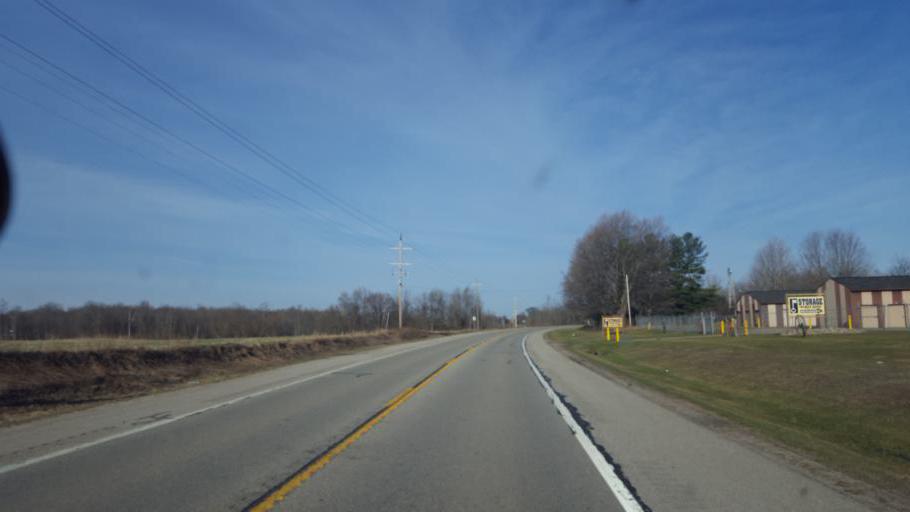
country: US
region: Michigan
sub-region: Montcalm County
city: Edmore
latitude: 43.4080
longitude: -85.1098
